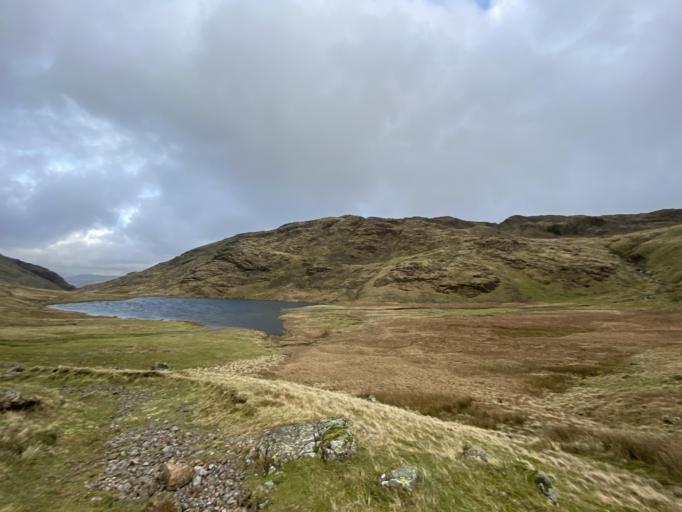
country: GB
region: England
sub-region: Cumbria
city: Keswick
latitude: 54.4769
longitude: -3.2050
